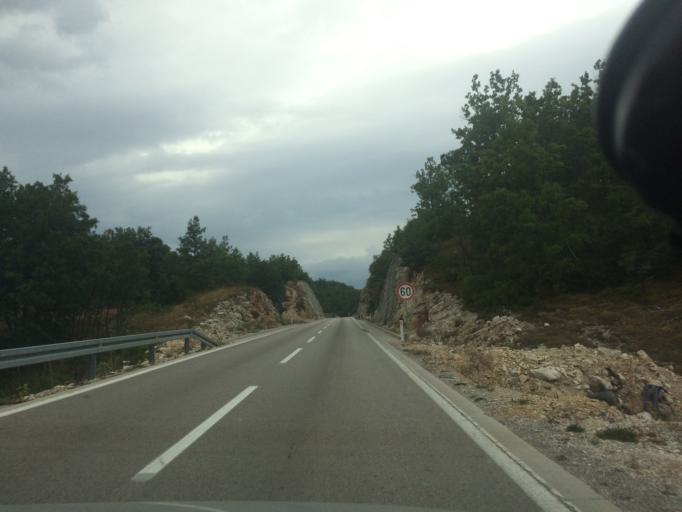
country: ME
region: Kotor
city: Risan
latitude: 42.7091
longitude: 18.6093
